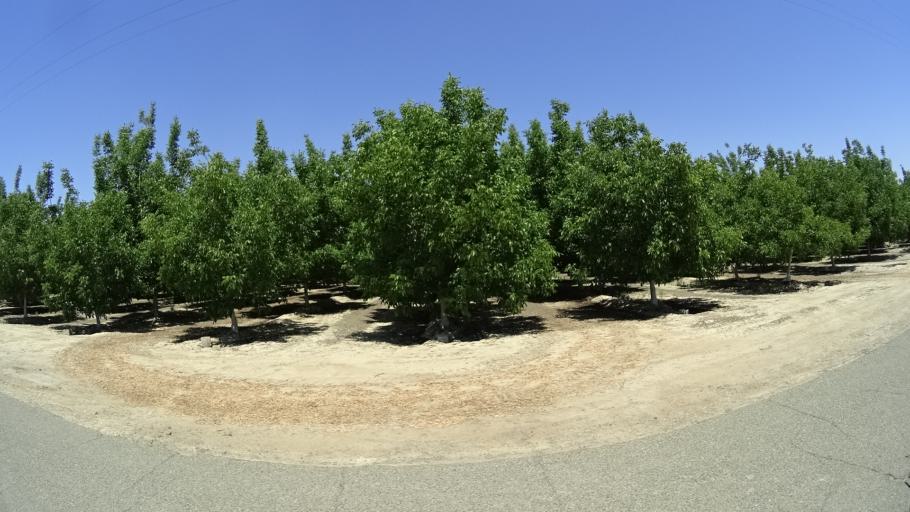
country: US
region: California
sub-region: Fresno County
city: Kingsburg
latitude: 36.4452
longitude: -119.5884
